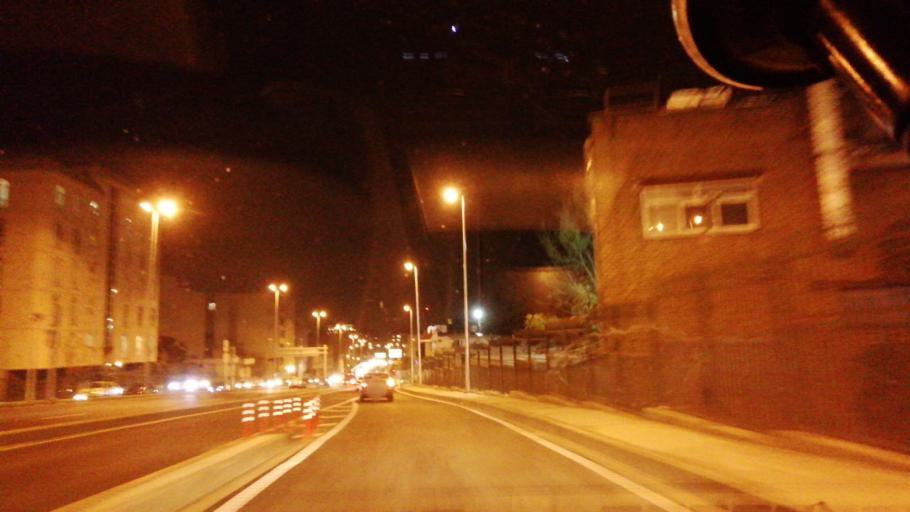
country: IR
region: Tehran
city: Tajrish
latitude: 35.7951
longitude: 51.4892
